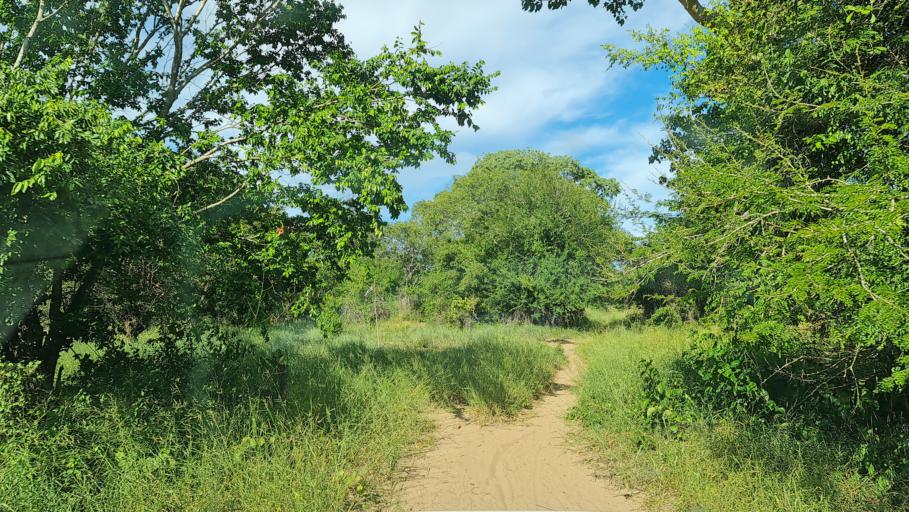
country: MZ
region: Nampula
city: Ilha de Mocambique
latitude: -15.5044
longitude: 40.1550
